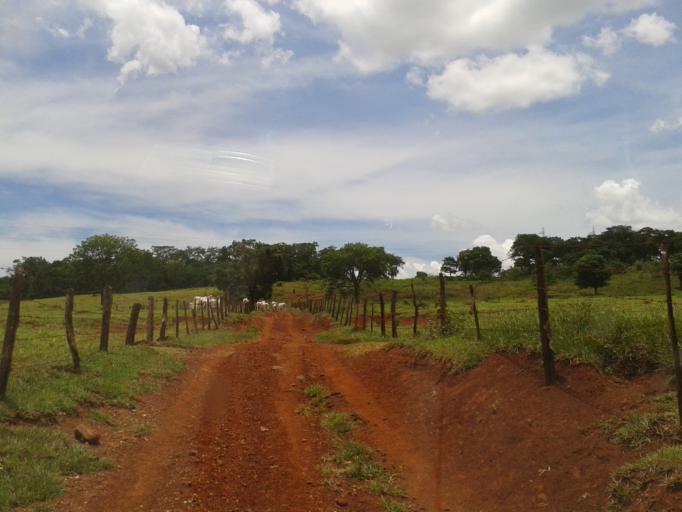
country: BR
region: Minas Gerais
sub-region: Centralina
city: Centralina
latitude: -18.6972
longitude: -49.2317
